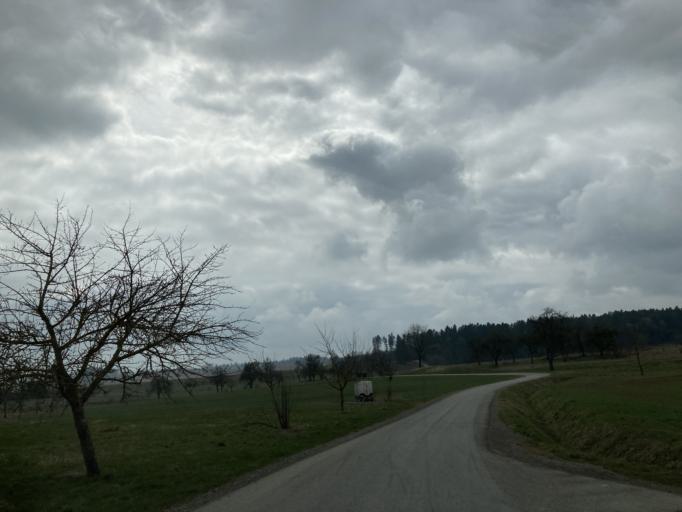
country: DE
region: Baden-Wuerttemberg
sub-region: Tuebingen Region
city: Haigerloch
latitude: 48.4263
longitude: 8.8139
